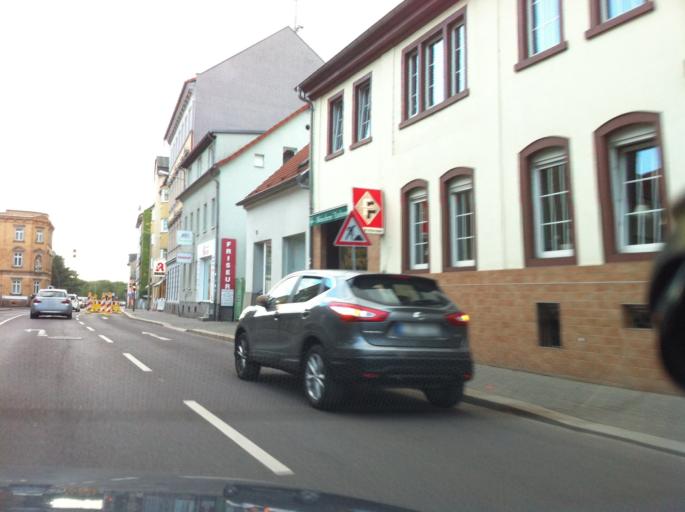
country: DE
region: Saxony
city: Markkleeberg
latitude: 51.3029
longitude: 12.3277
